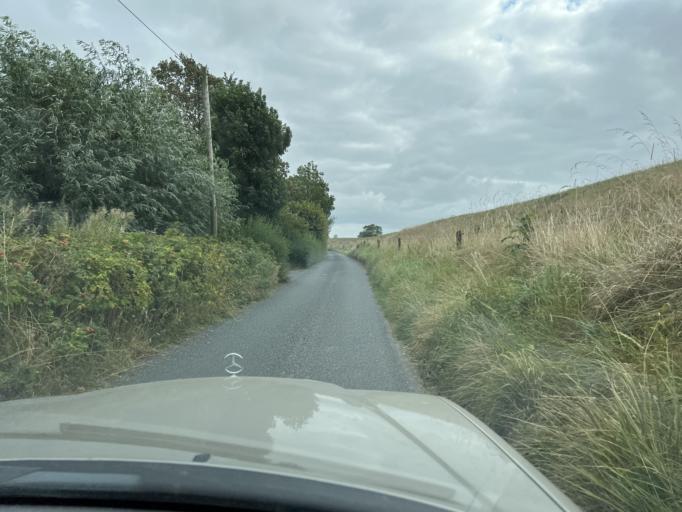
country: DE
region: Schleswig-Holstein
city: Groven
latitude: 54.3133
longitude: 8.9843
